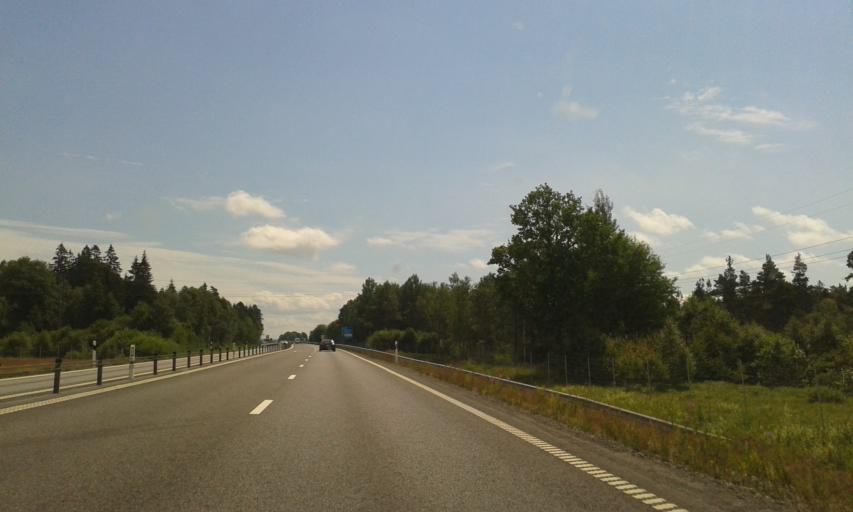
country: SE
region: Joenkoeping
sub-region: Varnamo Kommun
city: Varnamo
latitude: 57.1727
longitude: 14.0128
